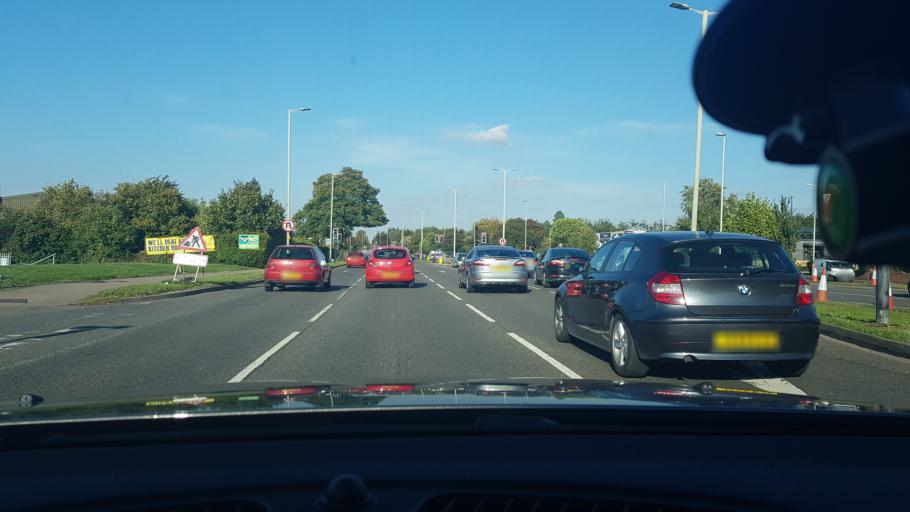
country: GB
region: England
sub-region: Gloucestershire
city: Barnwood
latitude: 51.8597
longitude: -2.2179
